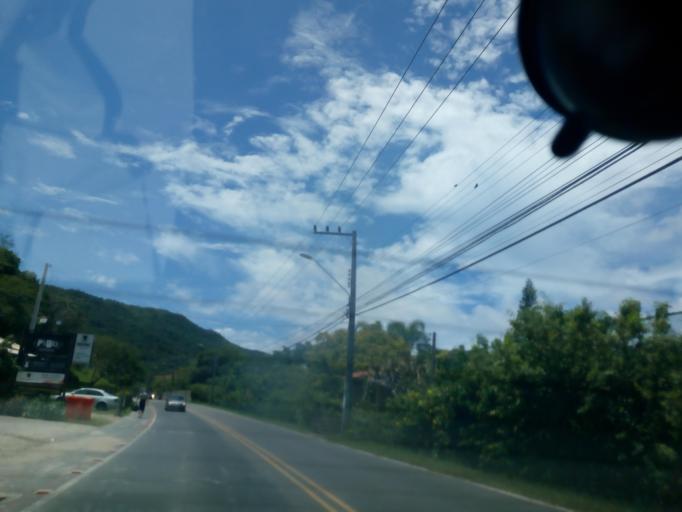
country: BR
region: Santa Catarina
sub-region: Florianopolis
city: Itacorubi
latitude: -27.4055
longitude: -48.4263
